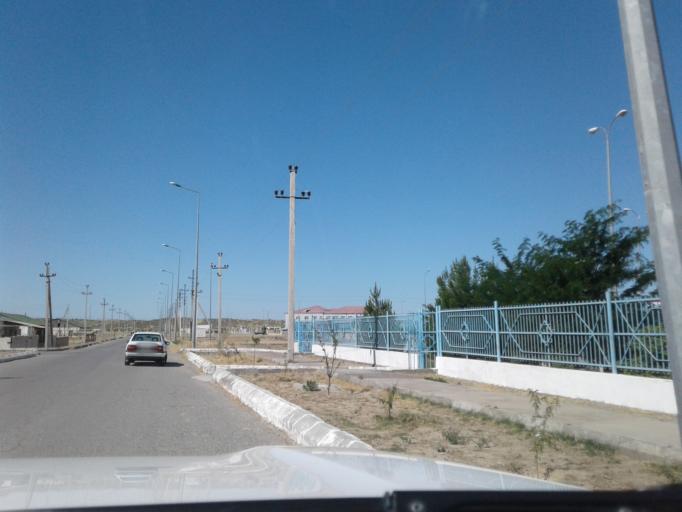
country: TM
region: Mary
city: Bayramaly
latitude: 38.0887
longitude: 62.7957
